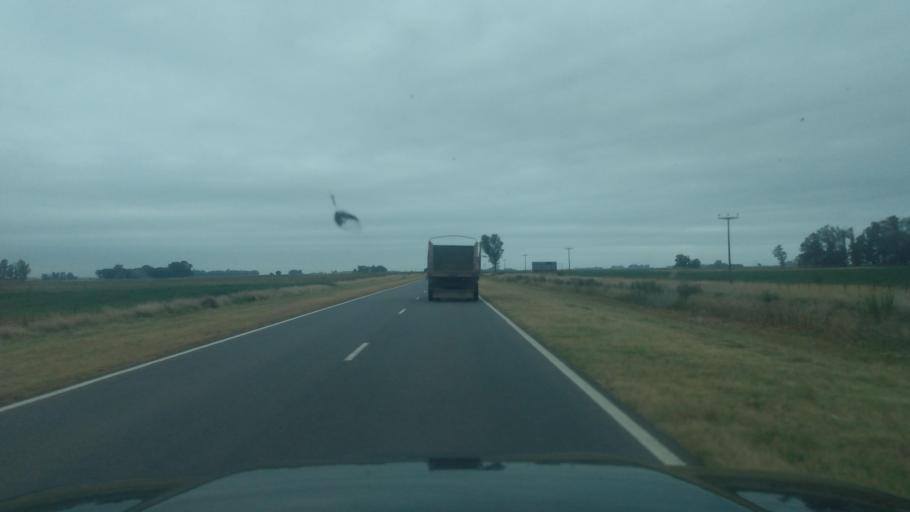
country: AR
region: Buenos Aires
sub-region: Partido de Nueve de Julio
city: Nueve de Julio
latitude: -35.3937
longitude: -60.7413
